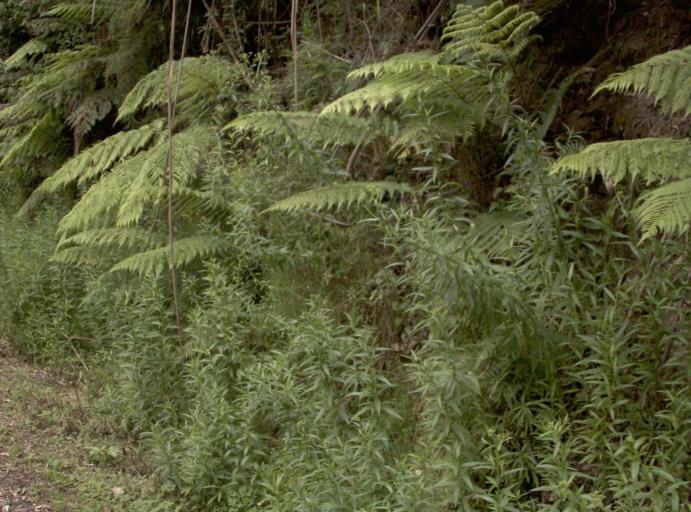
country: AU
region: Victoria
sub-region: Latrobe
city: Traralgon
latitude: -38.4533
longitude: 146.5406
